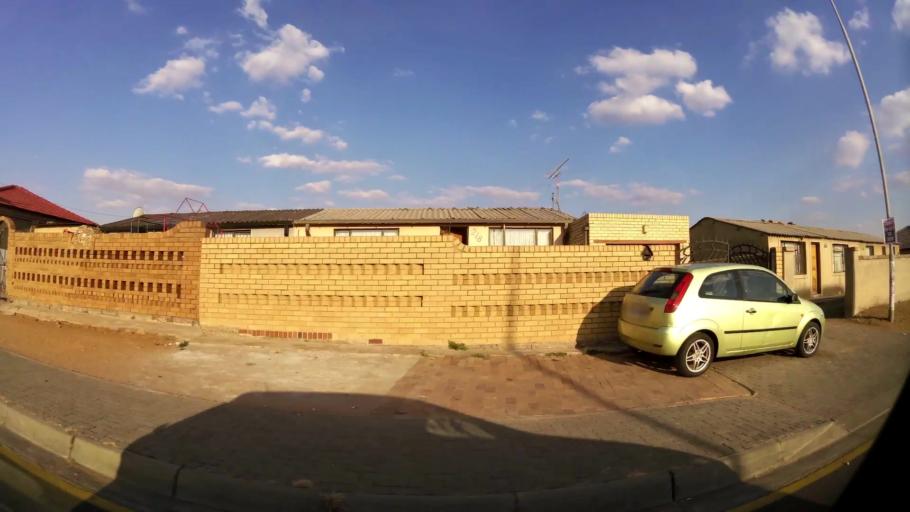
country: ZA
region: Gauteng
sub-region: City of Johannesburg Metropolitan Municipality
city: Roodepoort
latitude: -26.2133
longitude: 27.8913
